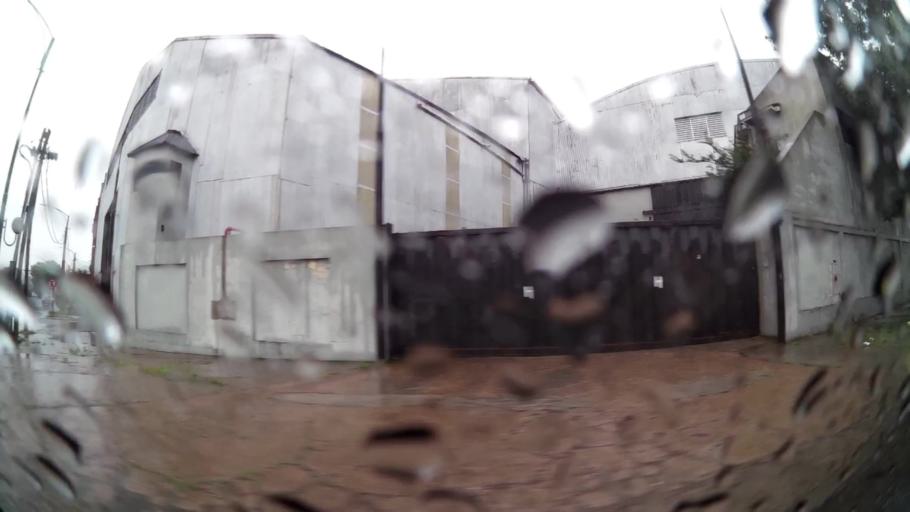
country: AR
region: Buenos Aires
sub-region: Partido de Avellaneda
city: Avellaneda
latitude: -34.6447
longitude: -58.3579
